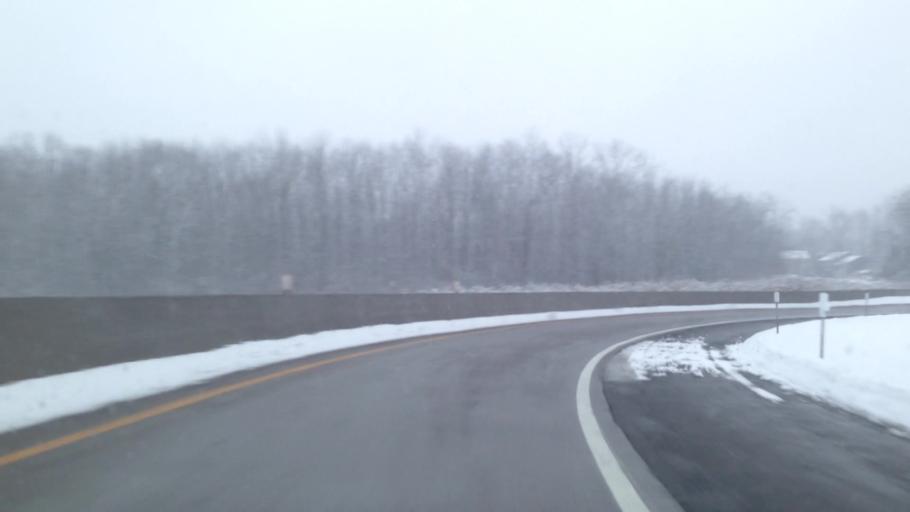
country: US
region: New York
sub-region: Onondaga County
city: East Syracuse
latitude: 43.0929
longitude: -76.0444
